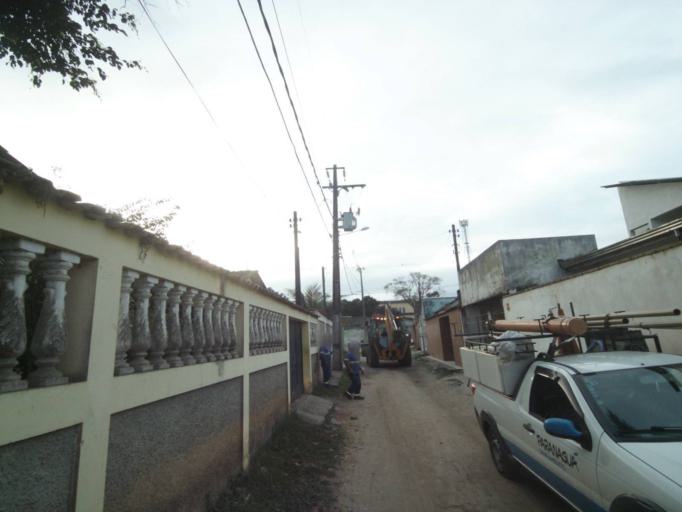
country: BR
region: Parana
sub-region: Paranagua
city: Paranagua
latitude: -25.5361
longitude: -48.5479
